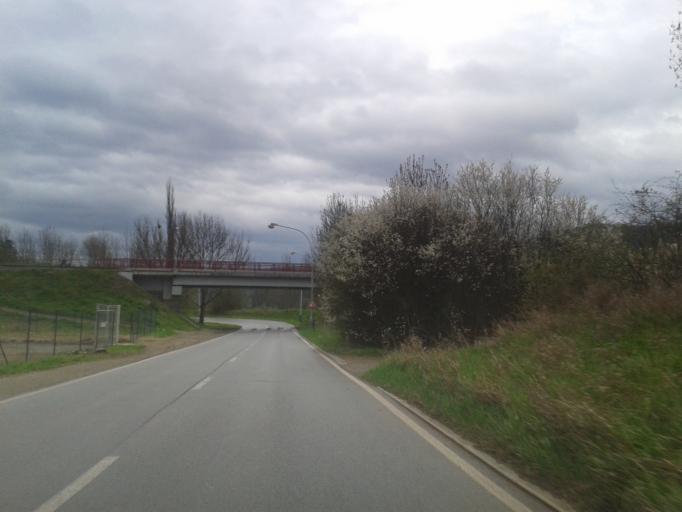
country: CZ
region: Central Bohemia
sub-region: Okres Beroun
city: Beroun
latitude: 49.9616
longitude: 14.0866
